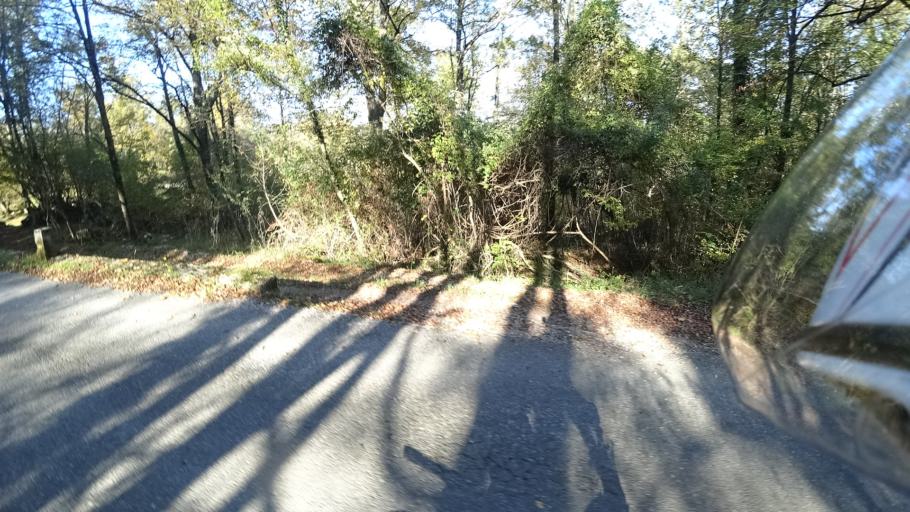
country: HR
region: Primorsko-Goranska
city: Matulji
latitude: 45.3822
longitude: 14.3016
